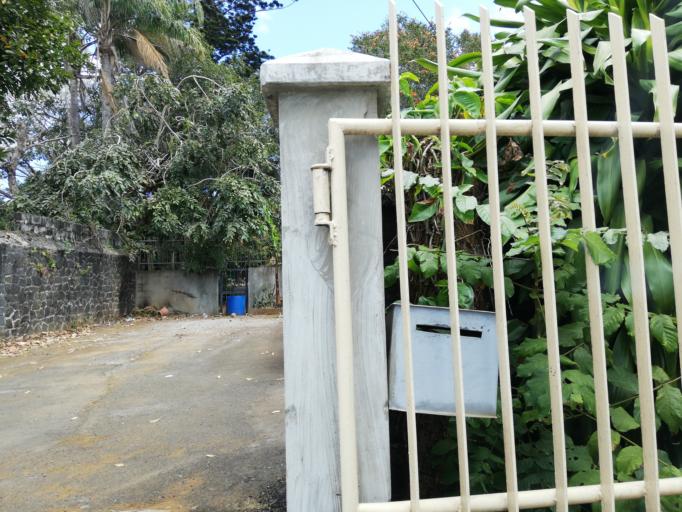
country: MU
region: Plaines Wilhems
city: Ebene
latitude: -20.2371
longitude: 57.4742
